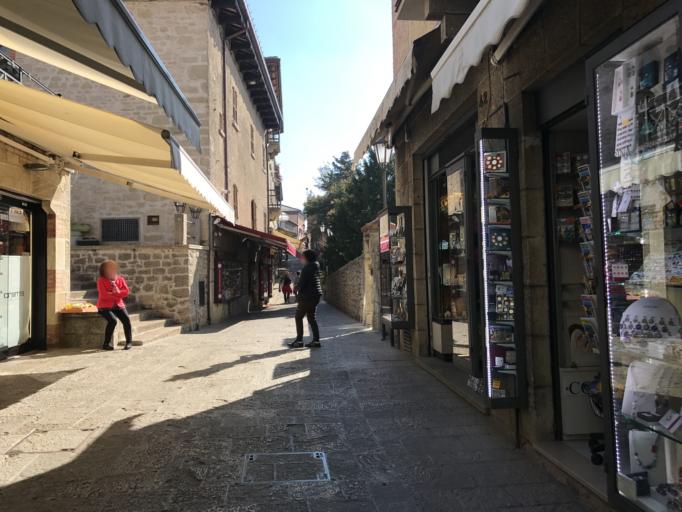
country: SM
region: San Marino
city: San Marino
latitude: 43.9361
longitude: 12.4477
